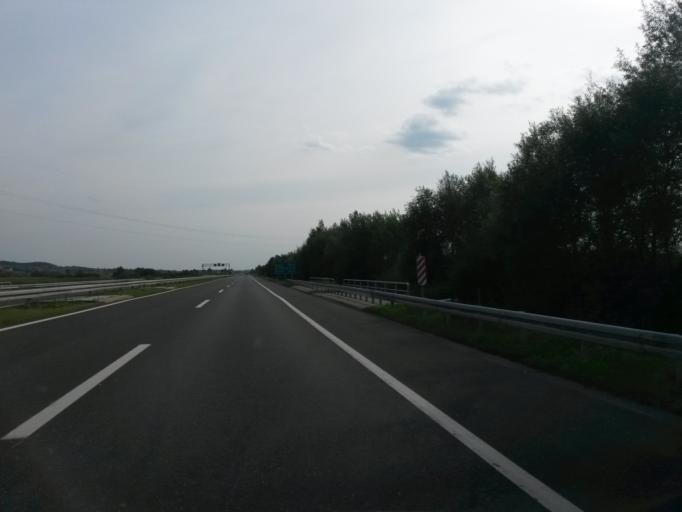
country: HR
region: Zagrebacka
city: Brckovljani
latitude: 45.9888
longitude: 16.2860
